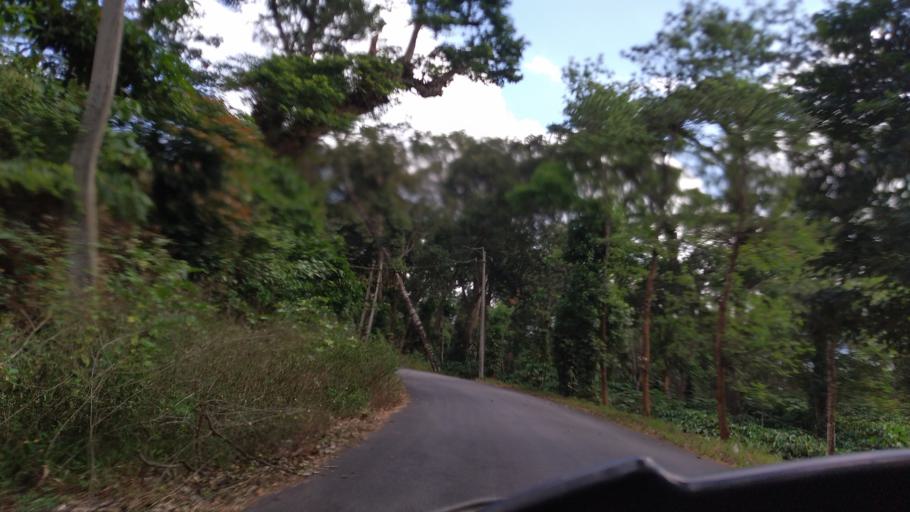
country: IN
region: Karnataka
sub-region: Kodagu
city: Ponnampet
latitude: 12.0315
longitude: 75.9242
